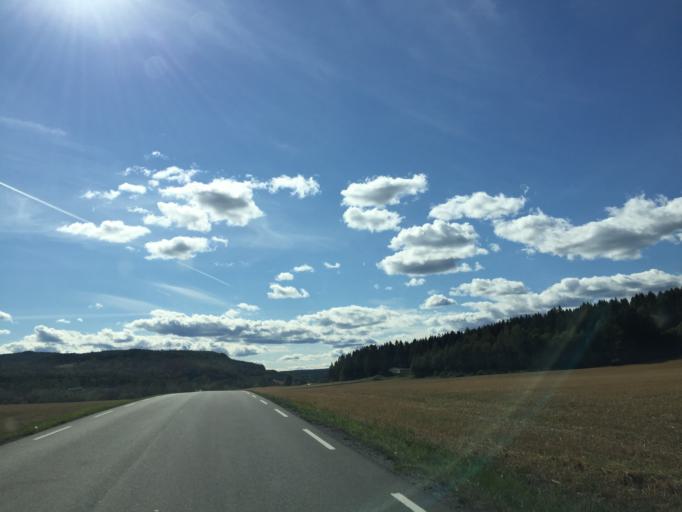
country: NO
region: Buskerud
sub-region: Ovre Eiker
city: Hokksund
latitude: 59.7051
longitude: 9.8571
